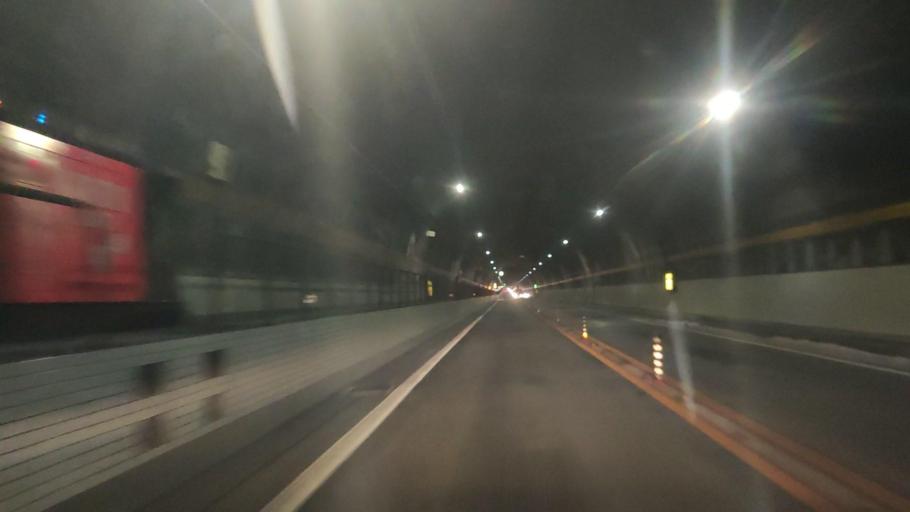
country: JP
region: Nagasaki
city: Obita
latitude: 32.7887
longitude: 129.8818
